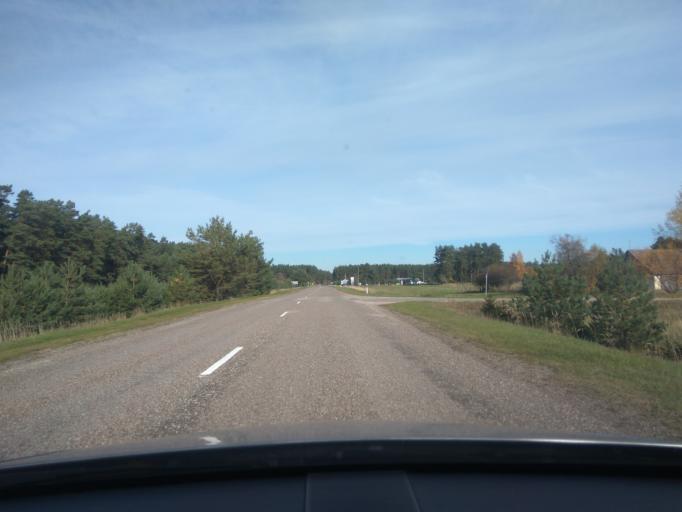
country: LV
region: Alsunga
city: Alsunga
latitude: 57.0094
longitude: 21.3892
